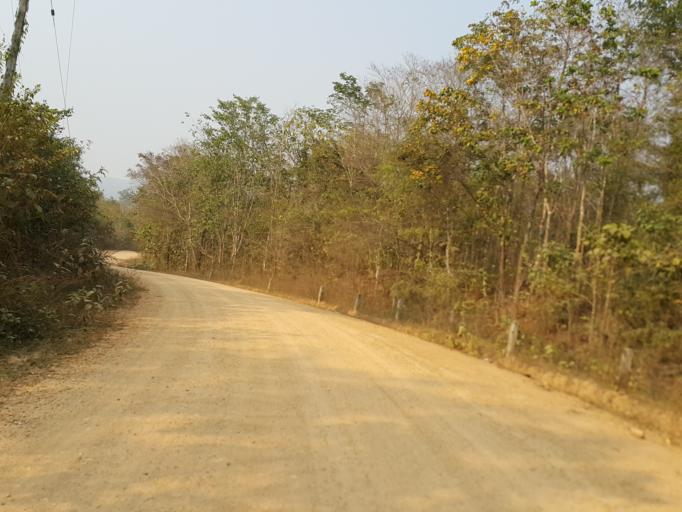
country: TH
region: Lampang
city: Mae Phrik
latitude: 17.5953
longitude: 98.9734
